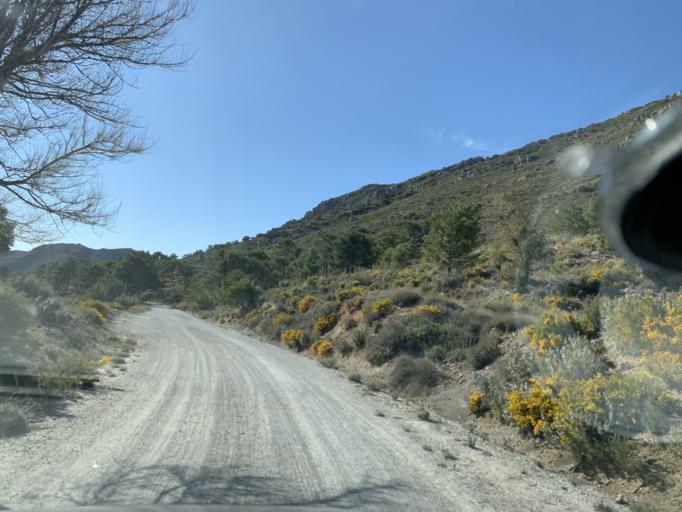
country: ES
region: Andalusia
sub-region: Provincia de Granada
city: Beas de Granada
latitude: 37.2419
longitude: -3.4494
